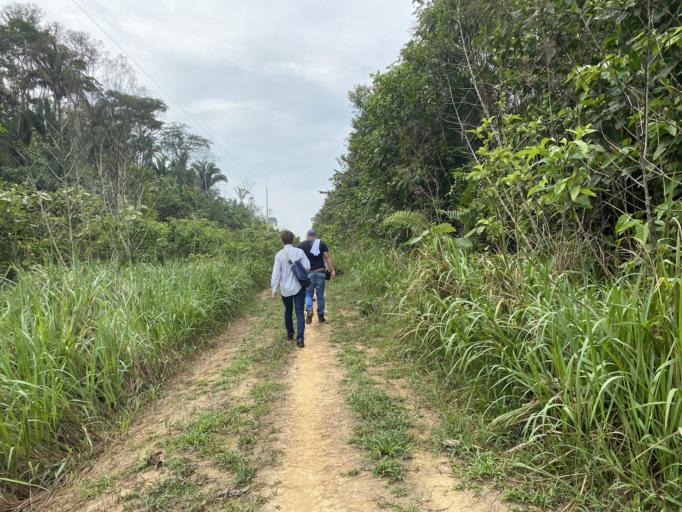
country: BR
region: Rondonia
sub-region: Porto Velho
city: Porto Velho
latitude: -8.8353
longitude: -64.2317
